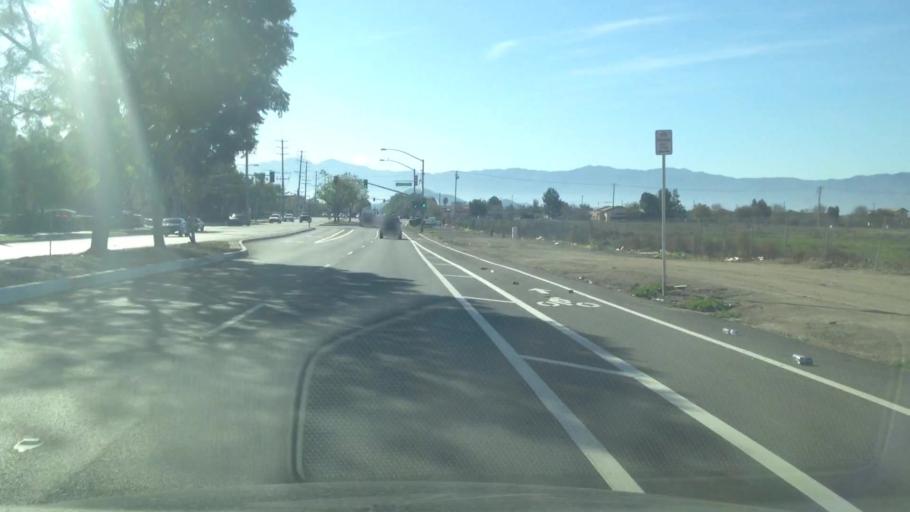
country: US
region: California
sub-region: Riverside County
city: Mira Loma
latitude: 33.9784
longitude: -117.5584
